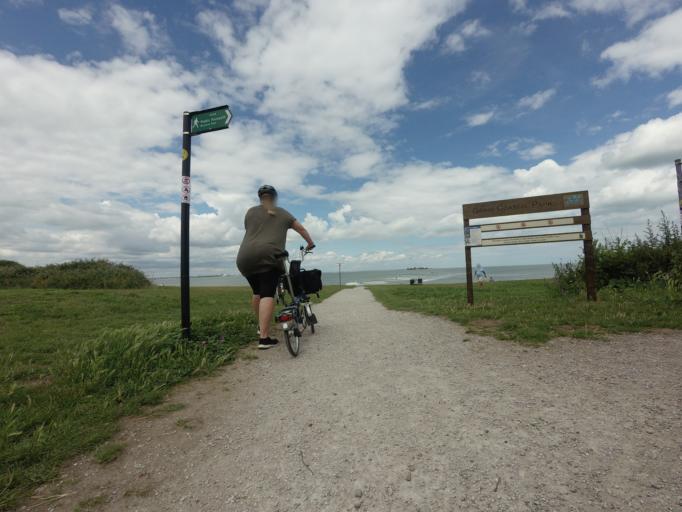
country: GB
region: England
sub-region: Kent
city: Sheerness
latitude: 51.4599
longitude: 0.7178
